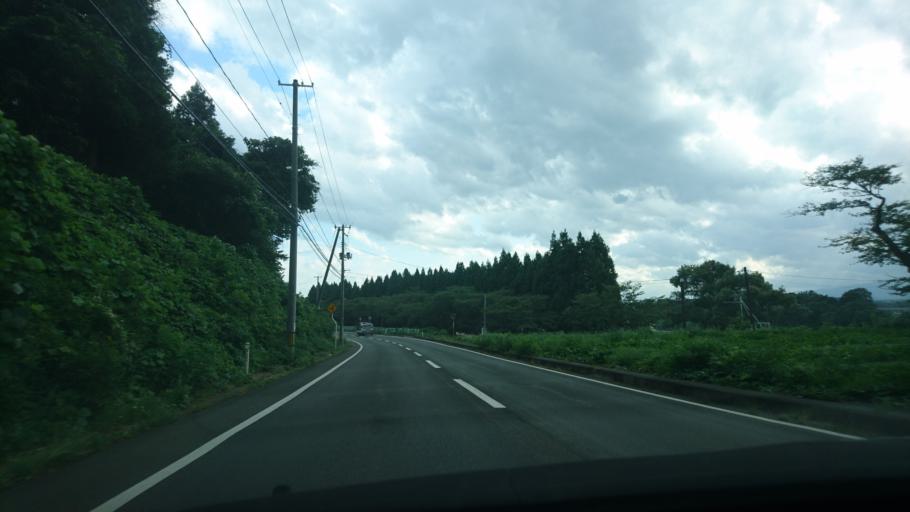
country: JP
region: Iwate
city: Kitakami
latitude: 39.2617
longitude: 141.1234
